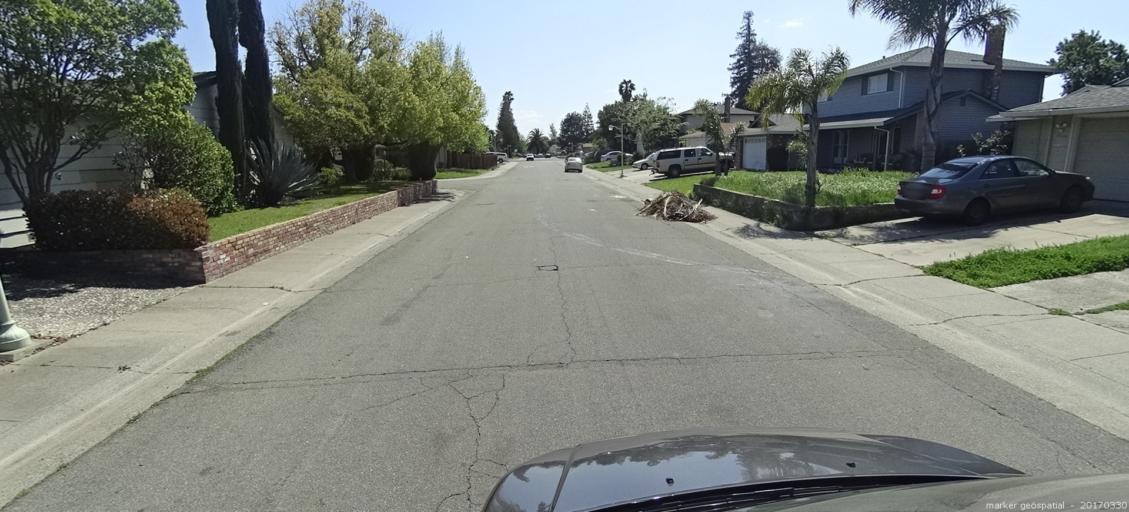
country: US
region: California
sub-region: Sacramento County
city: Florin
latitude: 38.4653
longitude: -121.4310
